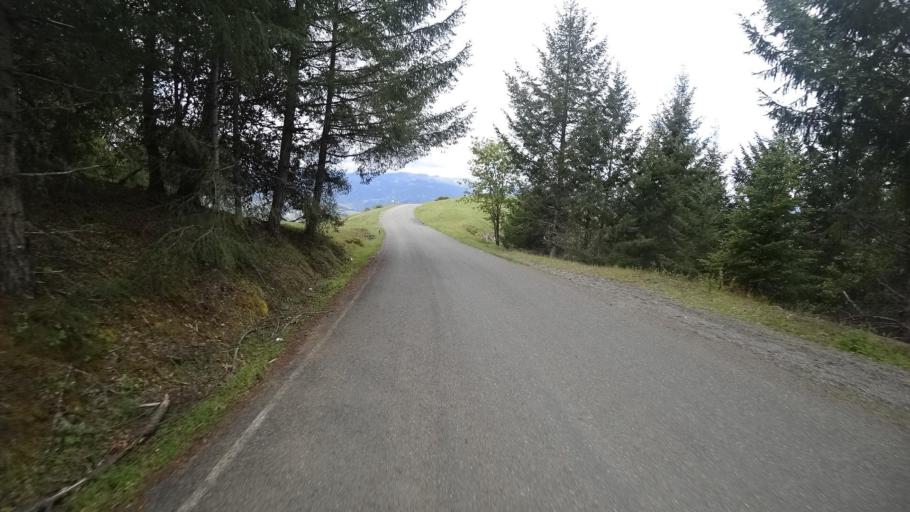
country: US
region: California
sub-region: Humboldt County
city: Redway
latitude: 40.1600
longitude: -123.5617
